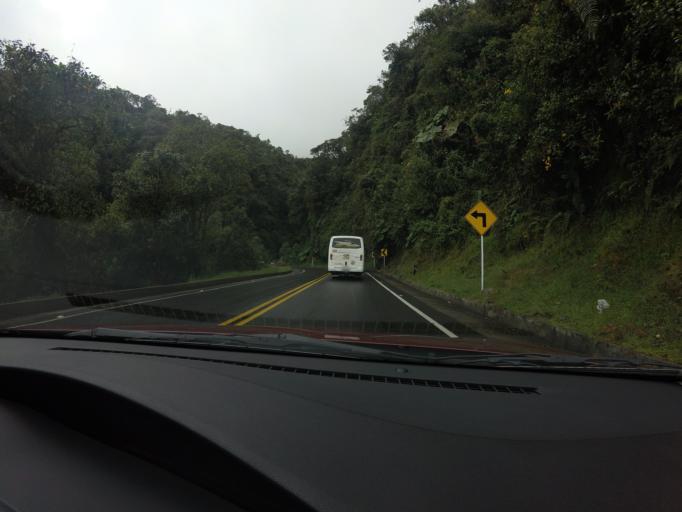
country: CO
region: Tolima
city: Herveo
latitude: 5.0959
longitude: -75.2781
